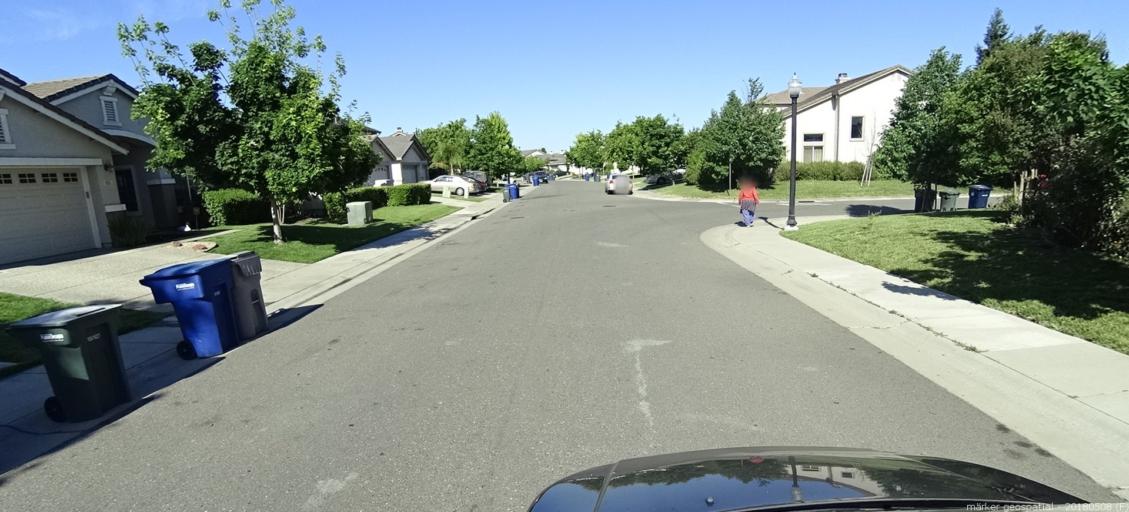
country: US
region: California
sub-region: Sacramento County
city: Elverta
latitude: 38.6779
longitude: -121.4964
